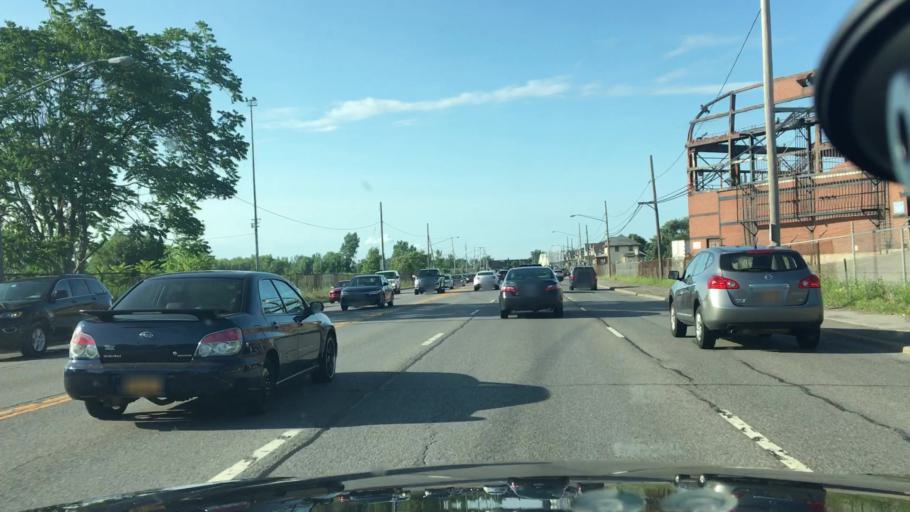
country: US
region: New York
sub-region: Erie County
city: Blasdell
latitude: 42.8085
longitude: -78.8461
